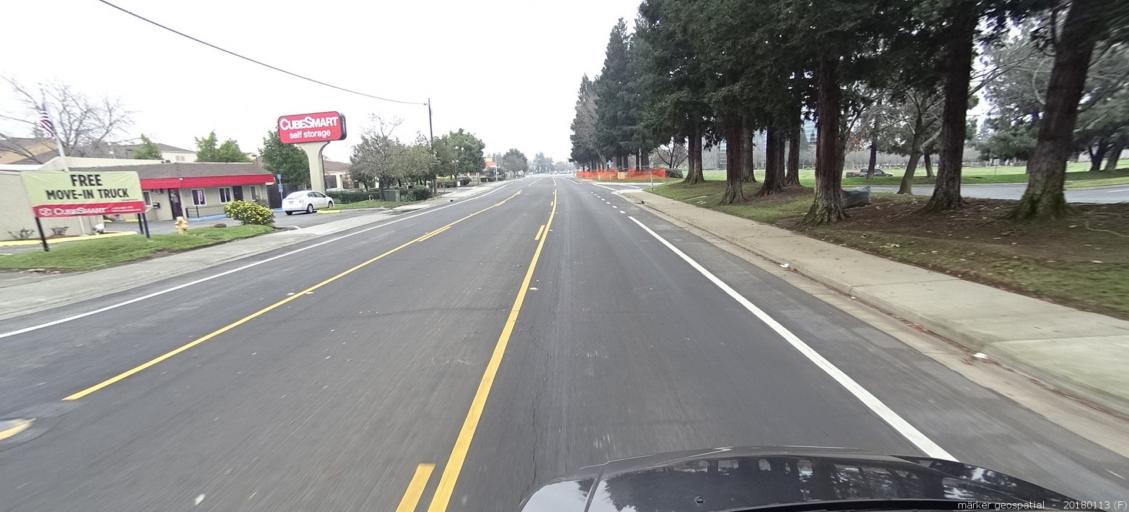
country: US
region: California
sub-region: Sacramento County
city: Rancho Cordova
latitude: 38.5869
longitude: -121.2912
